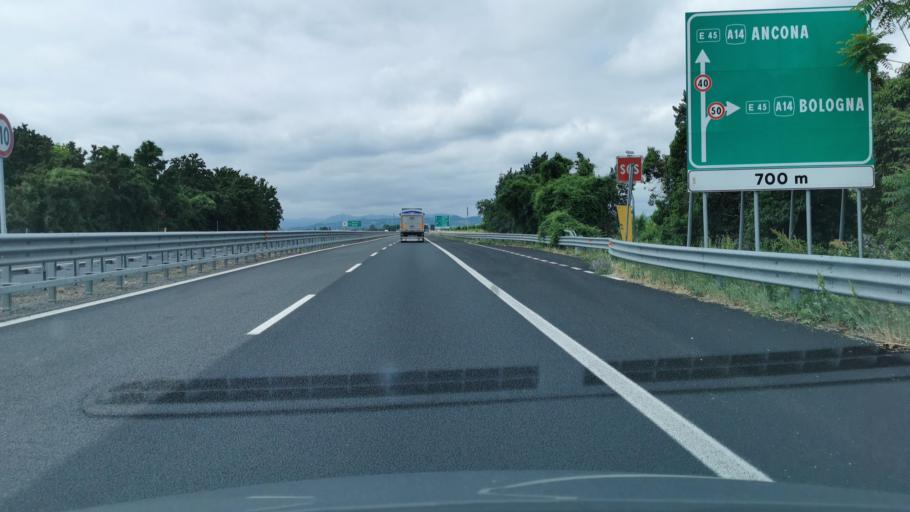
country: IT
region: Emilia-Romagna
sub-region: Provincia di Ravenna
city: Solarolo
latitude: 44.3616
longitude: 11.8247
